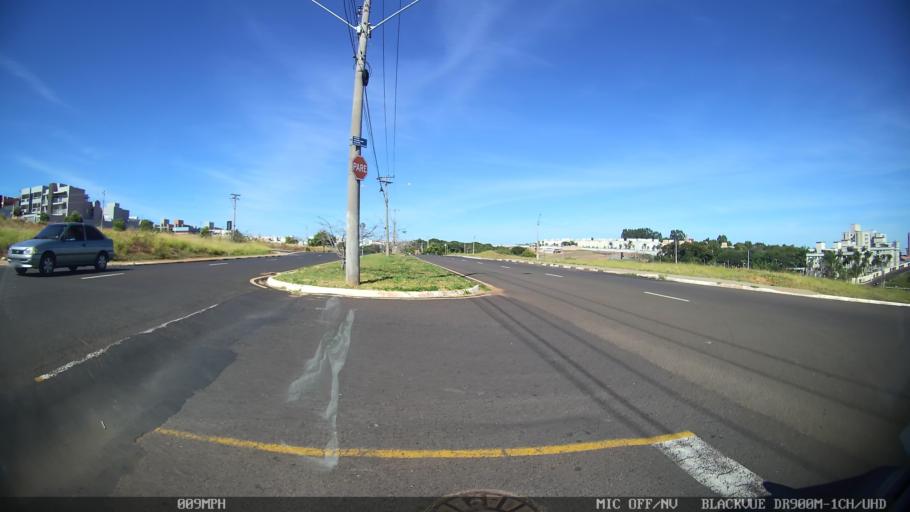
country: BR
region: Sao Paulo
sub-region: Franca
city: Franca
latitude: -20.5342
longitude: -47.3761
